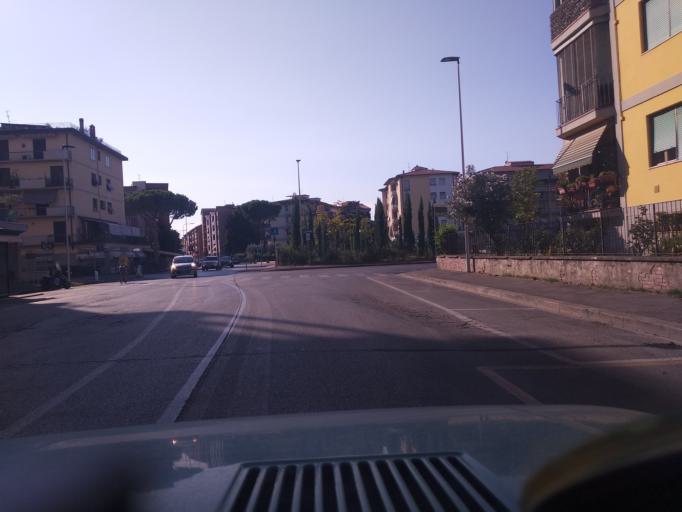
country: IT
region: Tuscany
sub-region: Province of Florence
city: Florence
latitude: 43.7779
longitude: 11.2132
